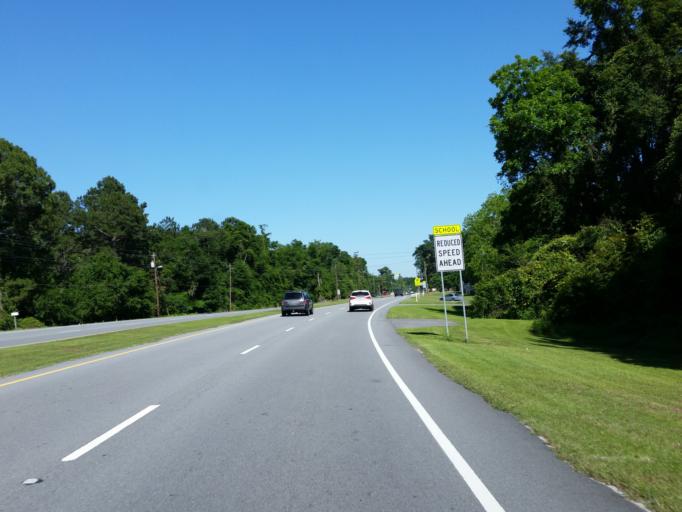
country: US
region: Georgia
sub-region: Echols County
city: Statenville
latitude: 30.6868
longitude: -83.1911
